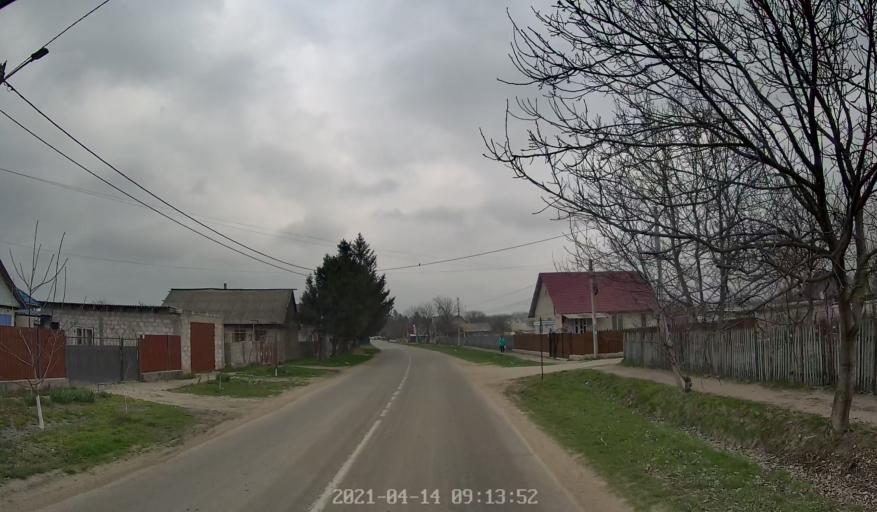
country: MD
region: Chisinau
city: Vadul lui Voda
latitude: 47.1049
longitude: 29.1137
